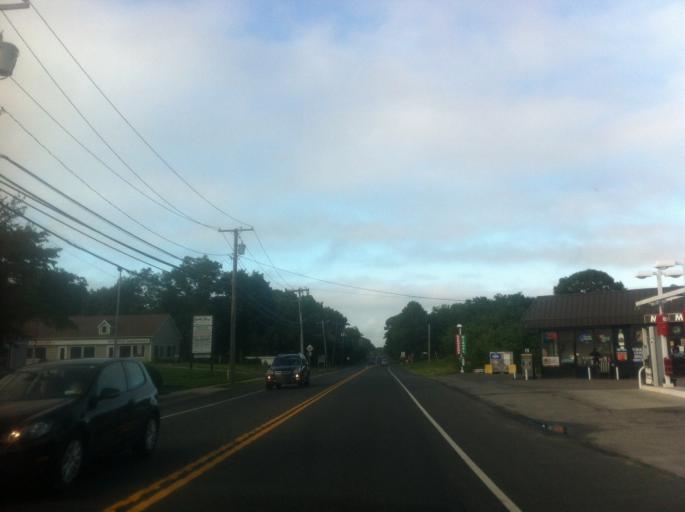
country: US
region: New York
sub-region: Suffolk County
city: Laurel
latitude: 40.9761
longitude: -72.5504
